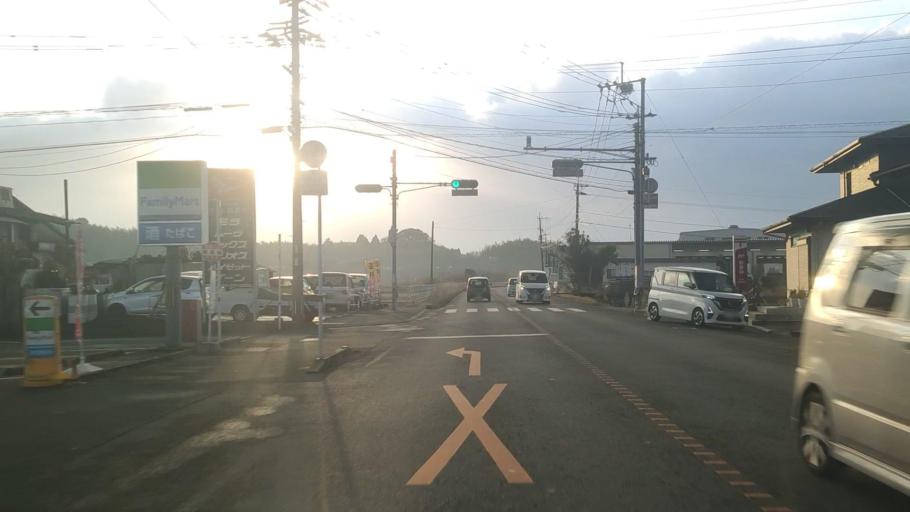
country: JP
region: Kumamoto
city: Uto
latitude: 32.7243
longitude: 130.7669
